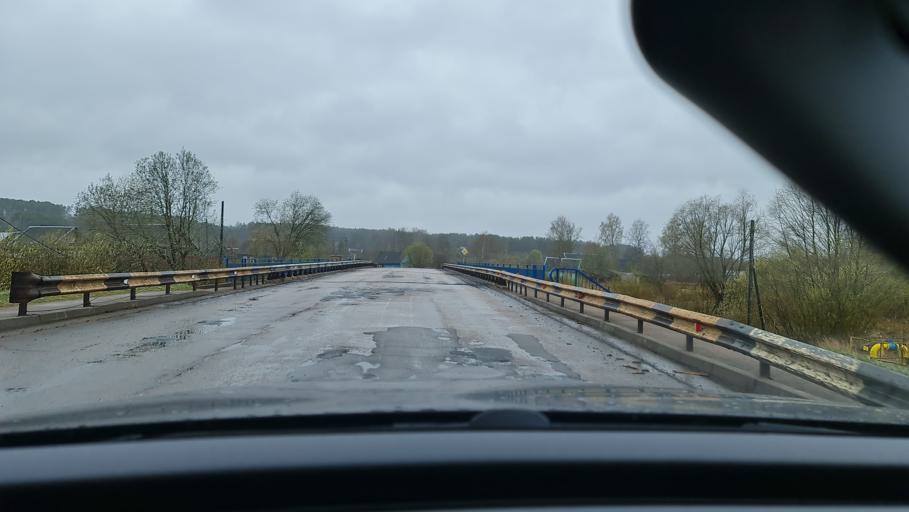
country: RU
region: Novgorod
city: Valday
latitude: 58.0358
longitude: 32.9499
